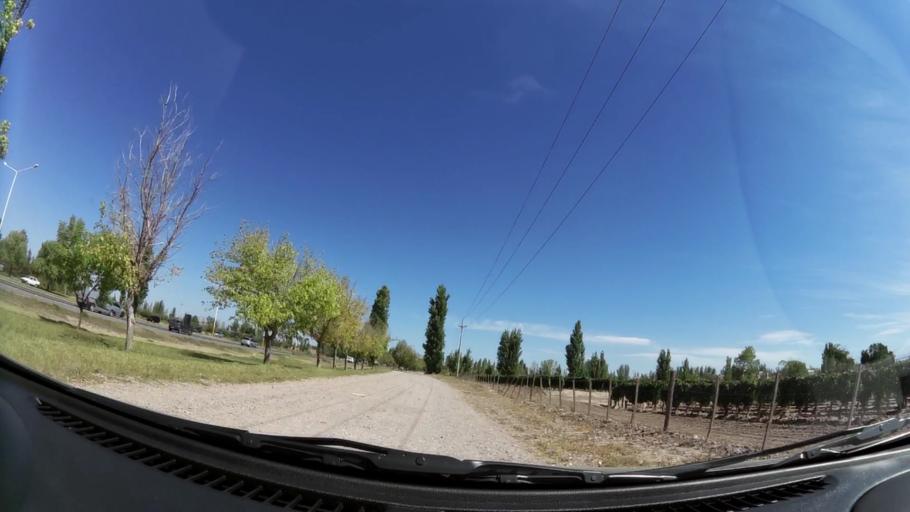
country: AR
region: Mendoza
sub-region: Departamento de Godoy Cruz
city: Godoy Cruz
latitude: -32.9805
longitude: -68.8485
